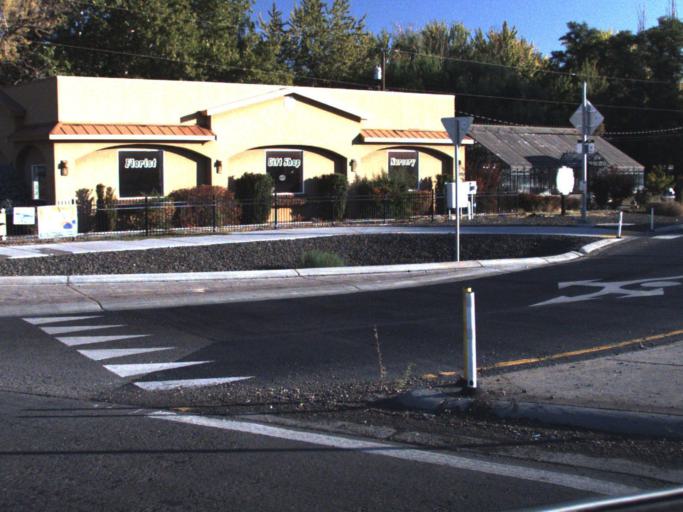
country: US
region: Washington
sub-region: Benton County
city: Benton City
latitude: 46.2518
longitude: -119.4751
